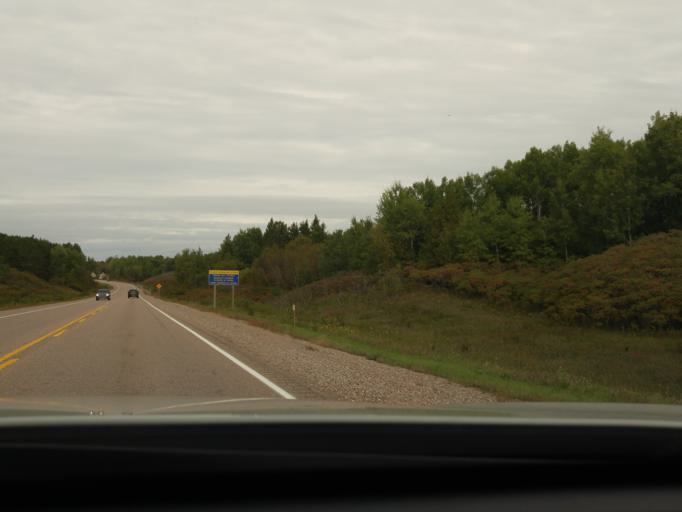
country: CA
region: Ontario
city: Renfrew
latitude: 45.5606
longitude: -76.7493
